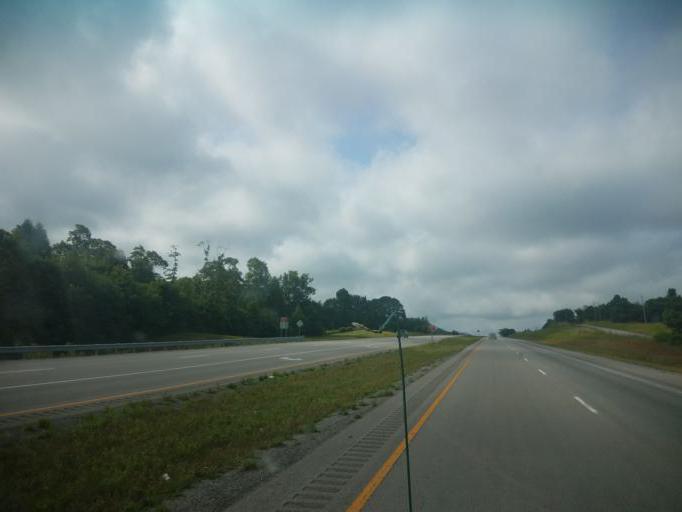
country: US
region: Kentucky
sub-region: Clinton County
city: Albany
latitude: 36.7498
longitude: -85.1364
